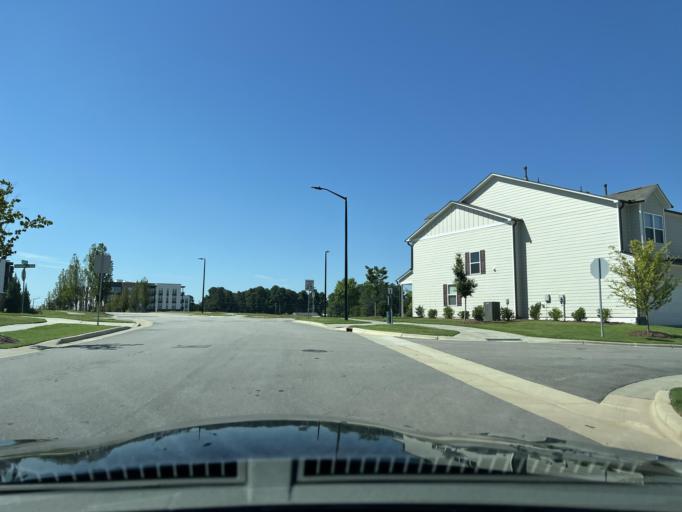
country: US
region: North Carolina
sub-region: Wake County
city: Morrisville
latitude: 35.8813
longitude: -78.8562
